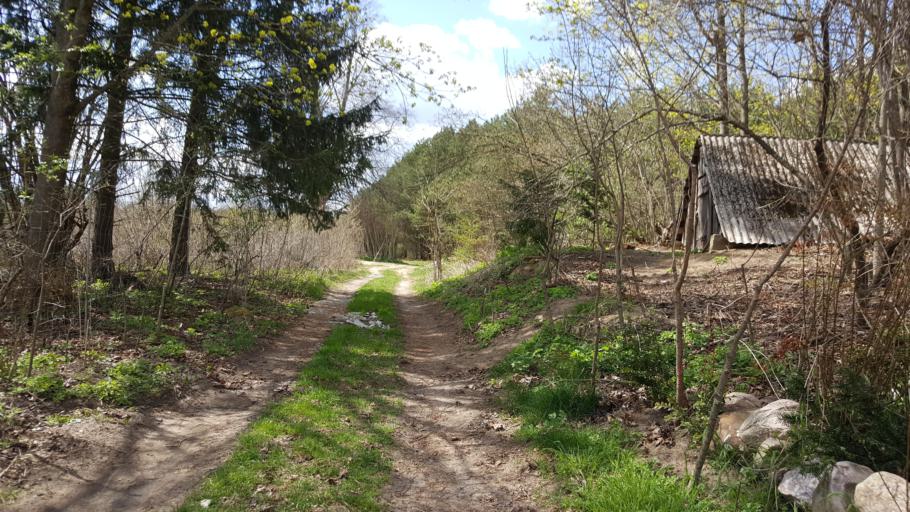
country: BY
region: Brest
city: Kamyanyets
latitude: 52.3528
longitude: 23.7044
